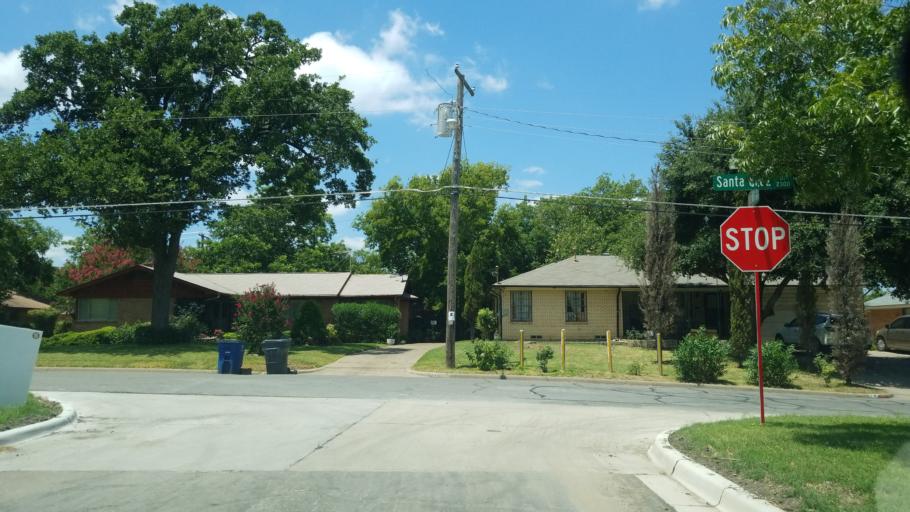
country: US
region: Texas
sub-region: Dallas County
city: Balch Springs
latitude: 32.7533
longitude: -96.6993
